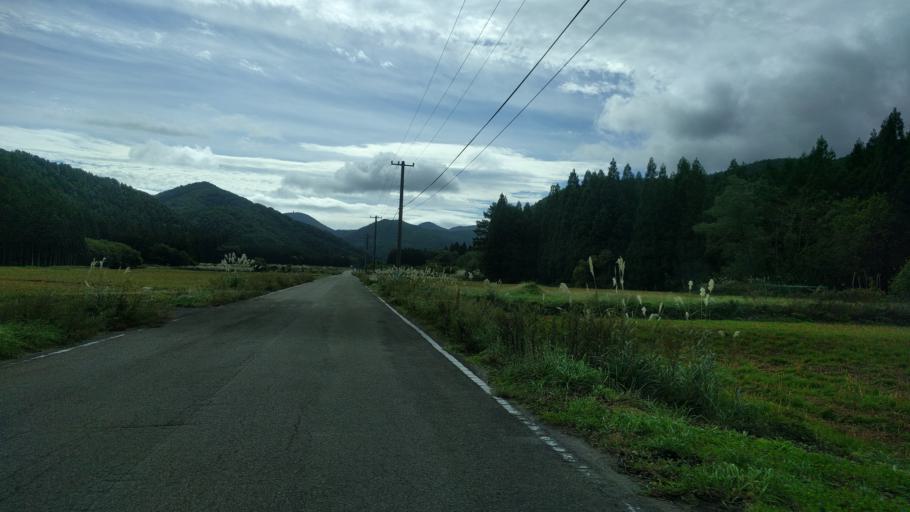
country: JP
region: Fukushima
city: Inawashiro
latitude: 37.3929
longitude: 140.1457
